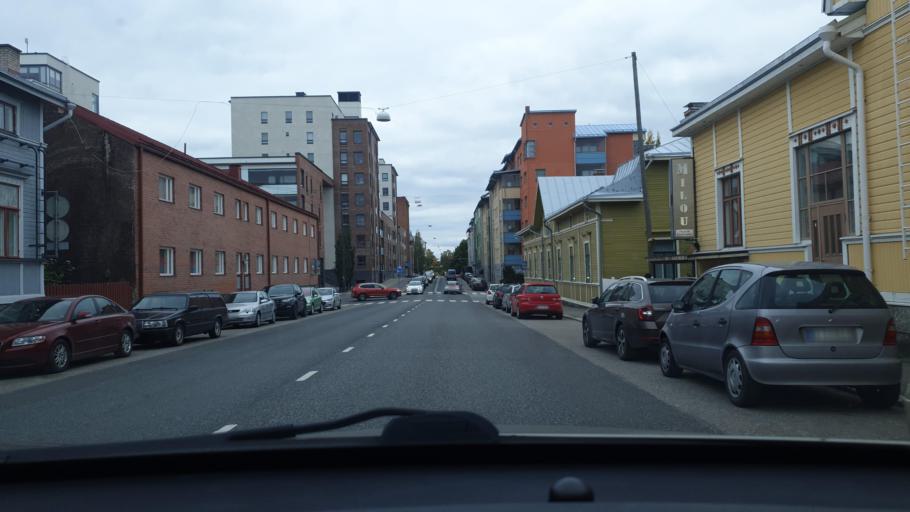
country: FI
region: Ostrobothnia
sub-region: Vaasa
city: Vaasa
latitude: 63.0940
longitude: 21.6240
